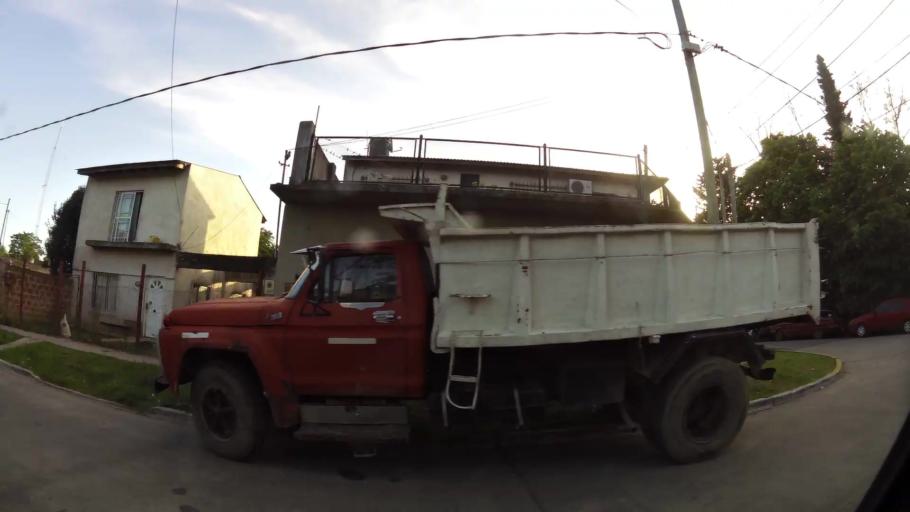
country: AR
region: Buenos Aires
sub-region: Partido de Quilmes
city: Quilmes
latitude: -34.7982
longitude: -58.1957
